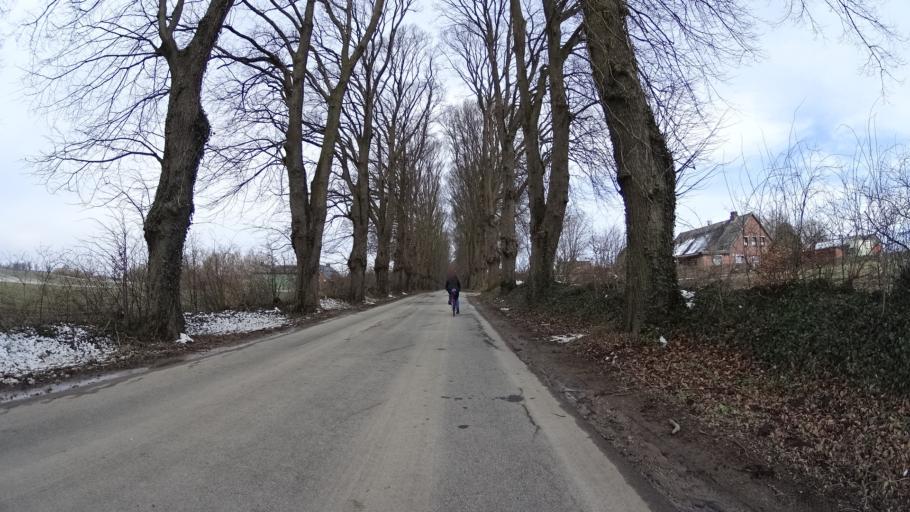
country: DE
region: Schleswig-Holstein
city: Rendswuhren
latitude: 54.0781
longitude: 10.1966
